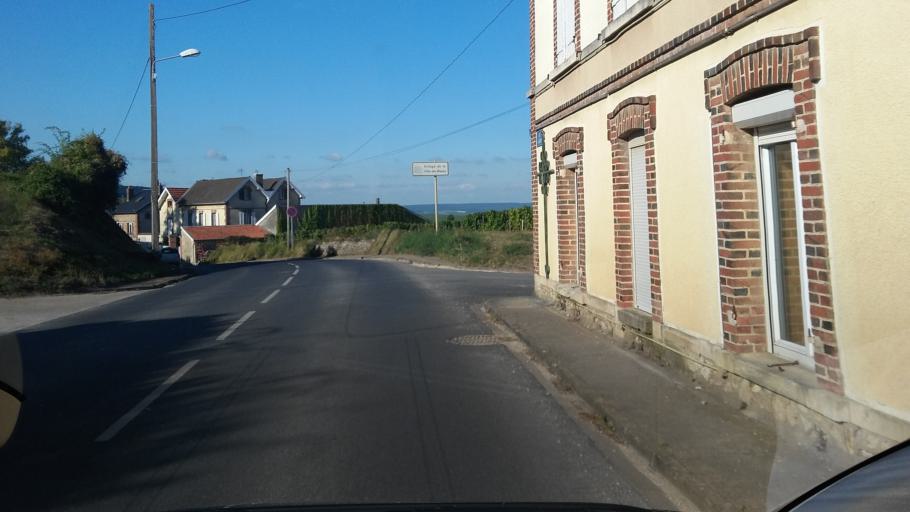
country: FR
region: Champagne-Ardenne
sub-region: Departement de la Marne
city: Avize
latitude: 48.9658
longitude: 4.0087
